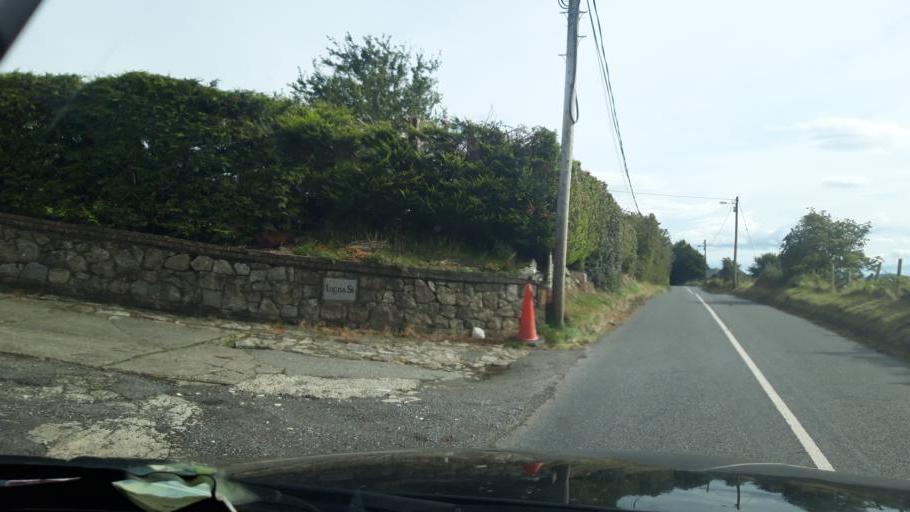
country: IE
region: Leinster
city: Balally
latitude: 53.2212
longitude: -6.2332
